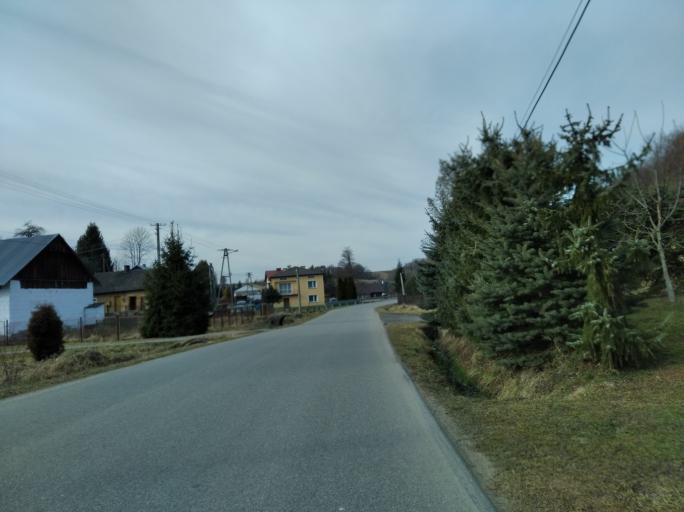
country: PL
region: Subcarpathian Voivodeship
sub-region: Powiat brzozowski
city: Gorki
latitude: 49.6418
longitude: 22.0523
